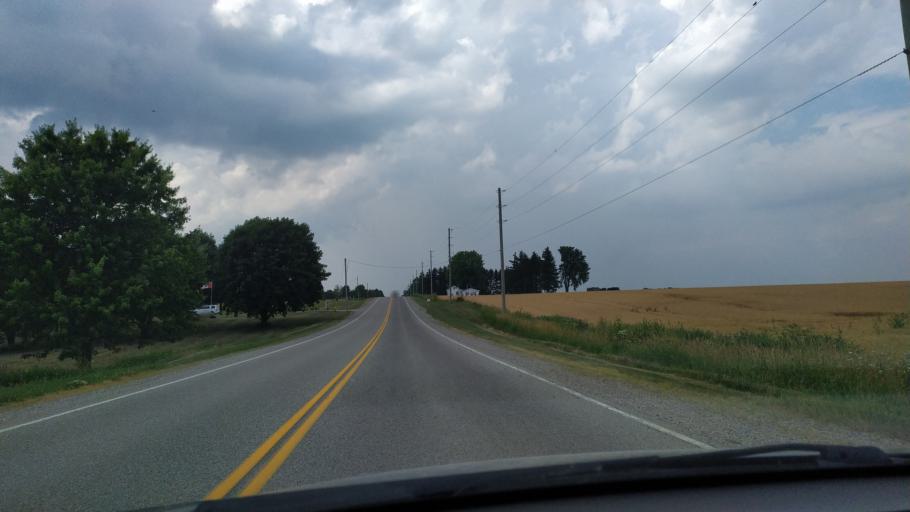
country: CA
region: Ontario
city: London
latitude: 43.1327
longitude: -81.1727
